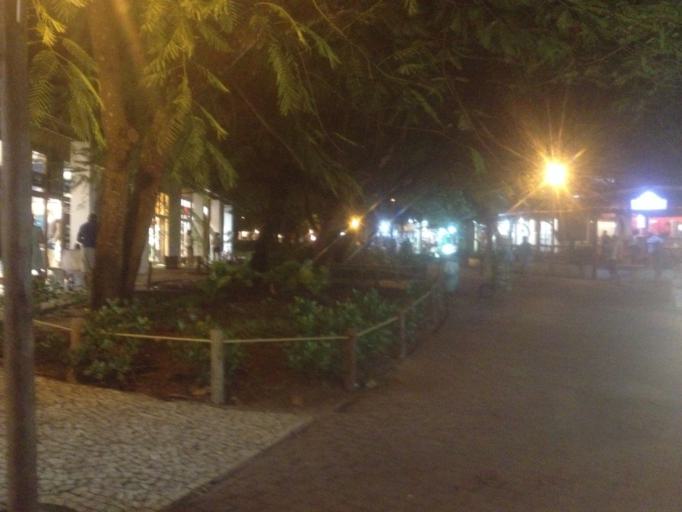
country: BR
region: Bahia
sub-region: Mata De Sao Joao
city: Mata de Sao Joao
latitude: -12.5774
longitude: -38.0038
